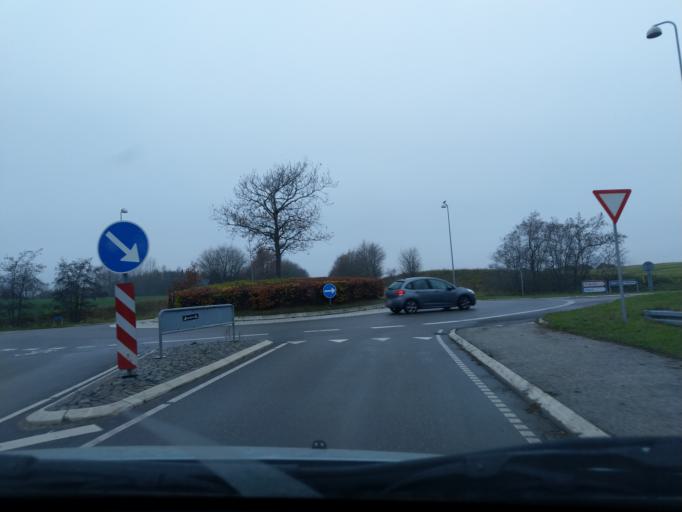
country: DK
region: Zealand
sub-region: Vordingborg Kommune
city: Praesto
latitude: 55.1143
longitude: 12.0326
